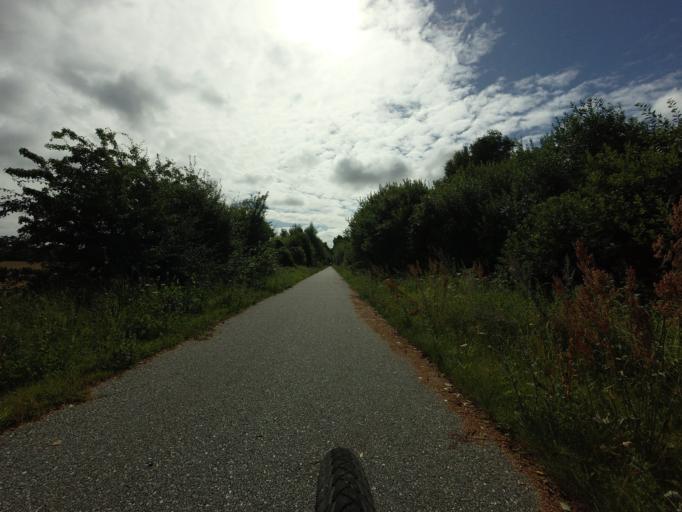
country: DK
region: Central Jutland
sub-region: Norddjurs Kommune
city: Auning
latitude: 56.4490
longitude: 10.3607
